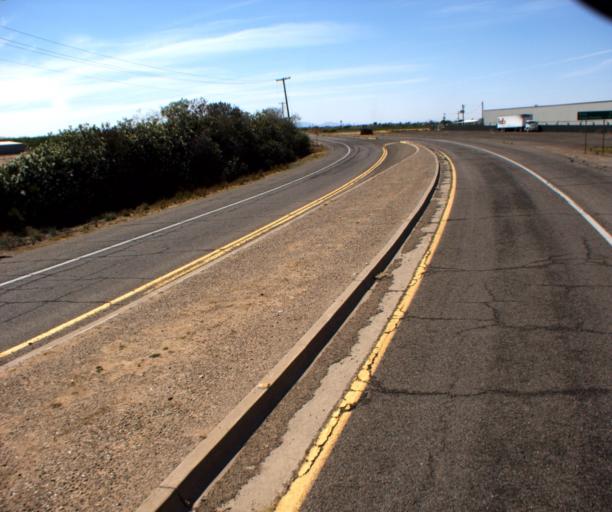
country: US
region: Arizona
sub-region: Pinal County
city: Eloy
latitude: 32.7340
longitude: -111.5177
